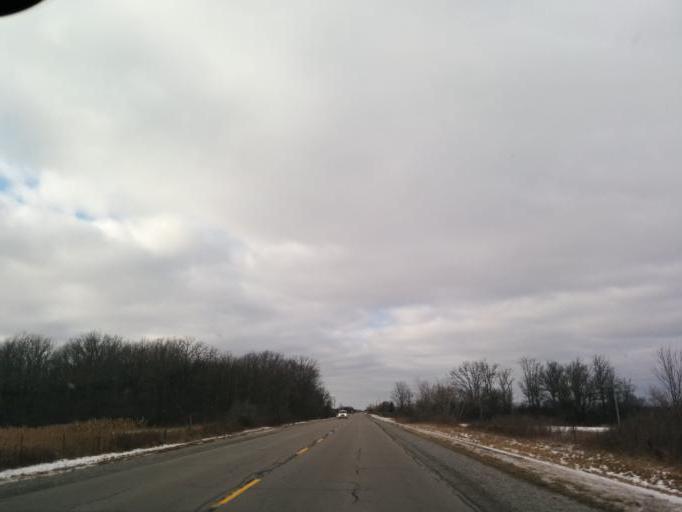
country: CA
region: Ontario
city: Brantford
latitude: 42.9834
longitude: -80.1096
